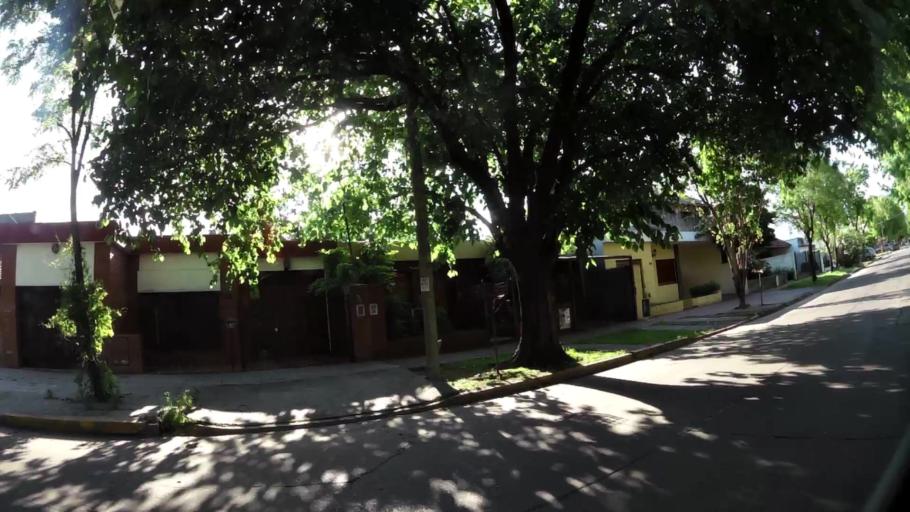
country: AR
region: Buenos Aires
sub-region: Partido de Merlo
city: Merlo
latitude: -34.6715
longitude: -58.7318
